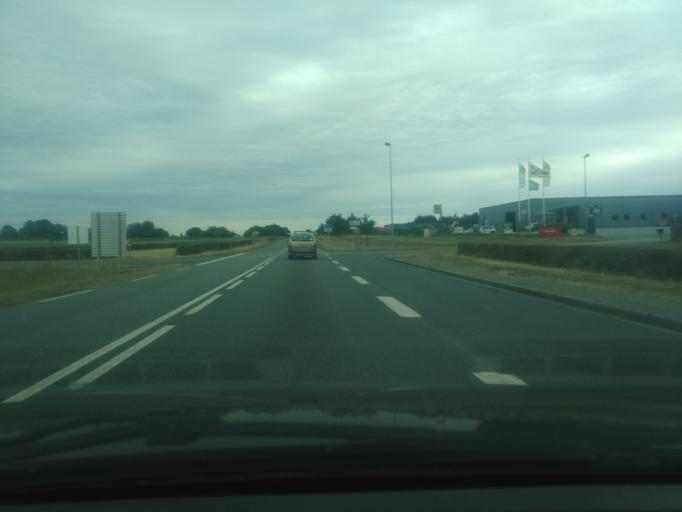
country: FR
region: Centre
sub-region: Departement de l'Indre
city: Saint-Marcel
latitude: 46.6230
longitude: 1.4902
